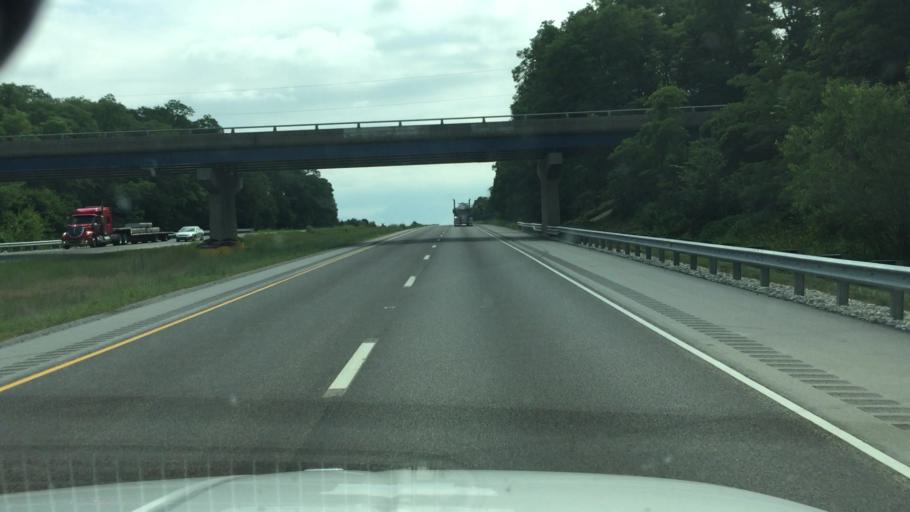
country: US
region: Illinois
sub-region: Peoria County
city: Elmwood
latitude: 40.8580
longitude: -90.0047
